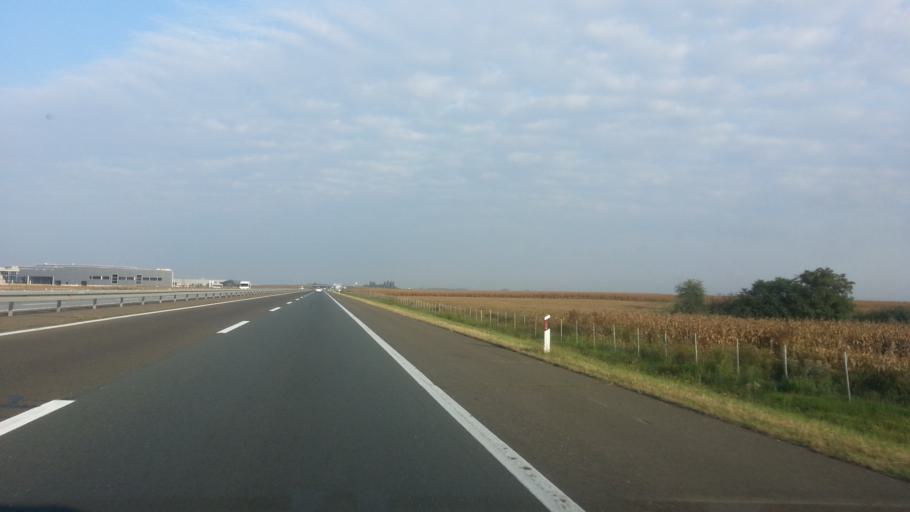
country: RS
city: Novi Banovci
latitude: 44.9610
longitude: 20.2501
